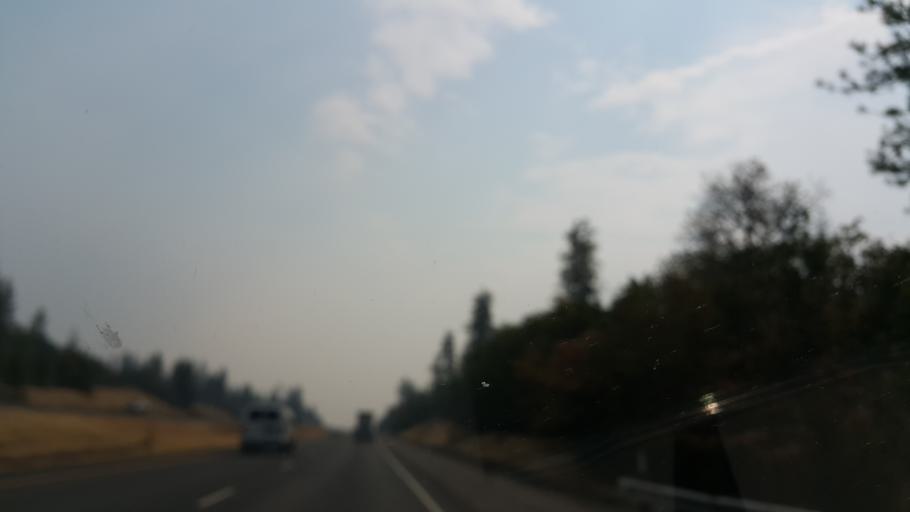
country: US
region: Oregon
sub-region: Josephine County
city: Merlin
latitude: 42.5501
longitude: -123.3712
